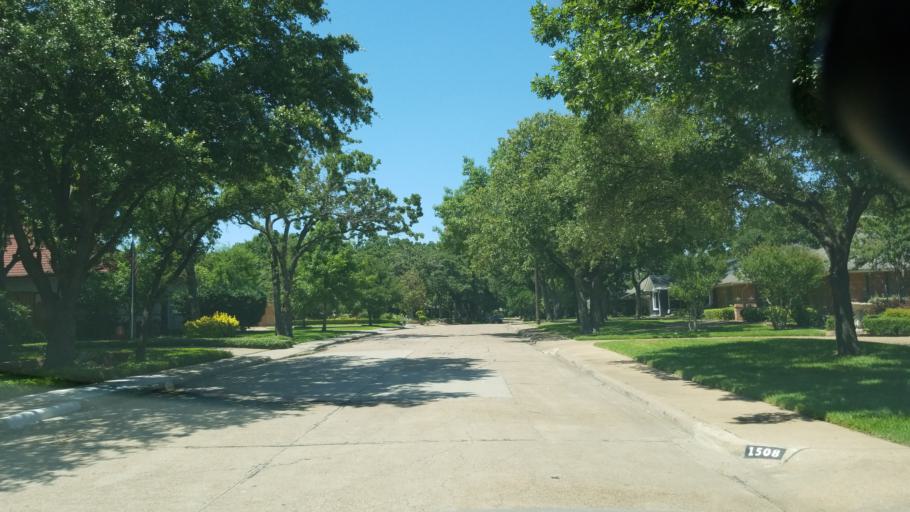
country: US
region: Texas
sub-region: Dallas County
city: Irving
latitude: 32.8294
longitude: -96.9655
